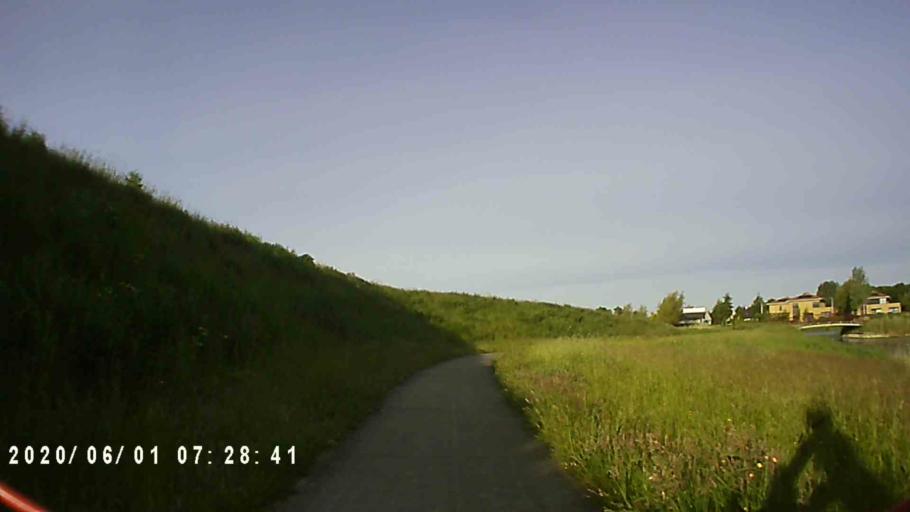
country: NL
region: Friesland
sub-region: Gemeente Dongeradeel
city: Dokkum
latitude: 53.3140
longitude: 6.0140
